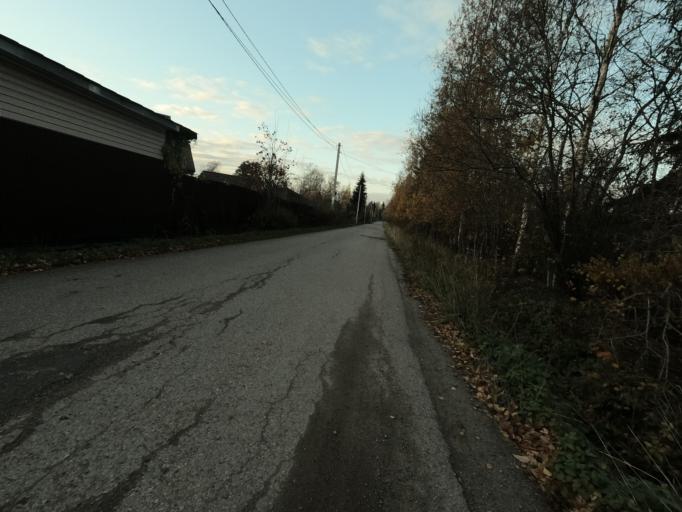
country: RU
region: Leningrad
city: Mga
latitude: 59.7778
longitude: 31.2054
